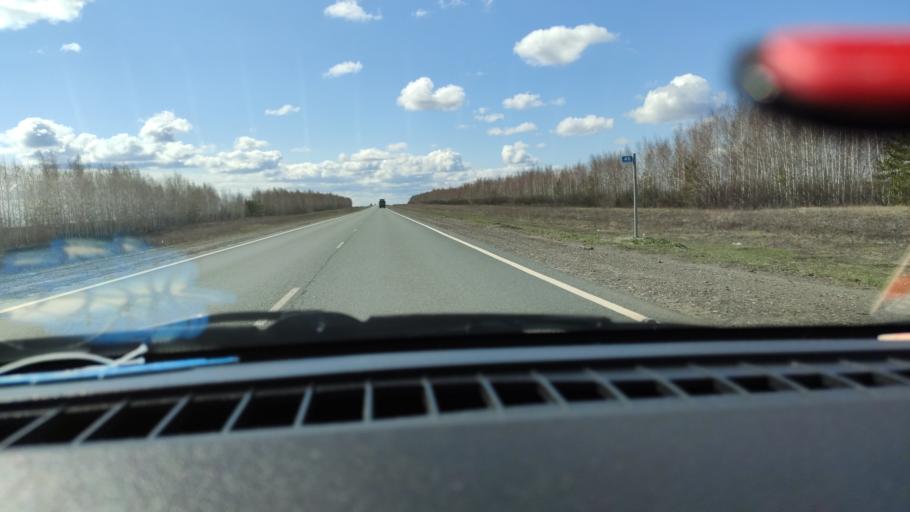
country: RU
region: Saratov
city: Dukhovnitskoye
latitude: 52.8145
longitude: 48.2312
